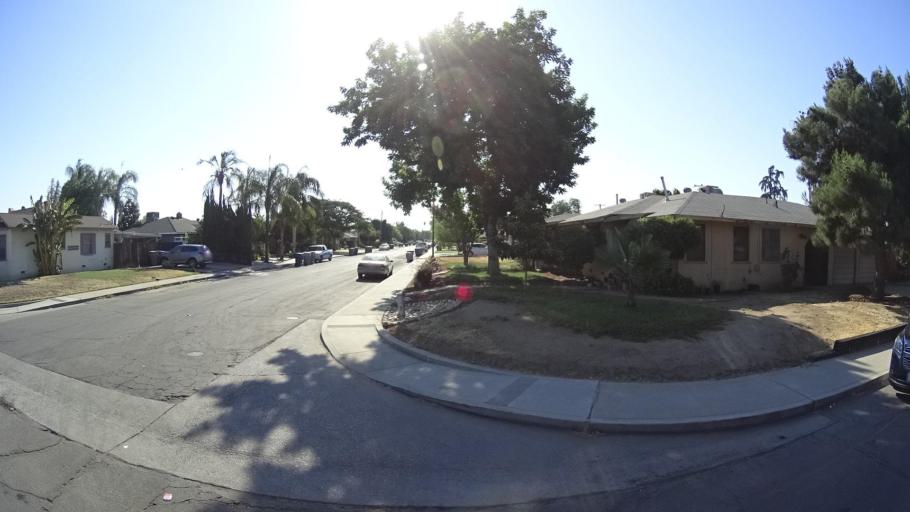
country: US
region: California
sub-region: Fresno County
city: Fresno
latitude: 36.7746
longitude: -119.7714
